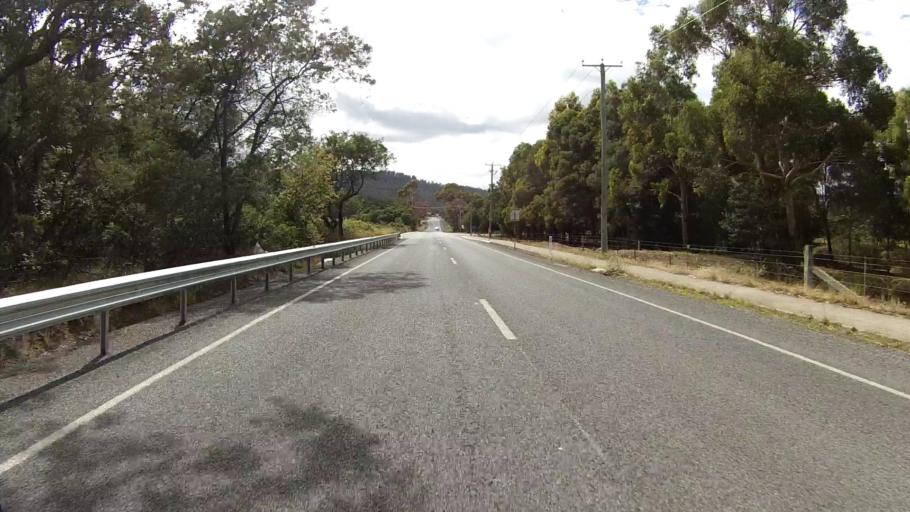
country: AU
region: Tasmania
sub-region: Glenorchy
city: Lutana
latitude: -42.8080
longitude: 147.3436
